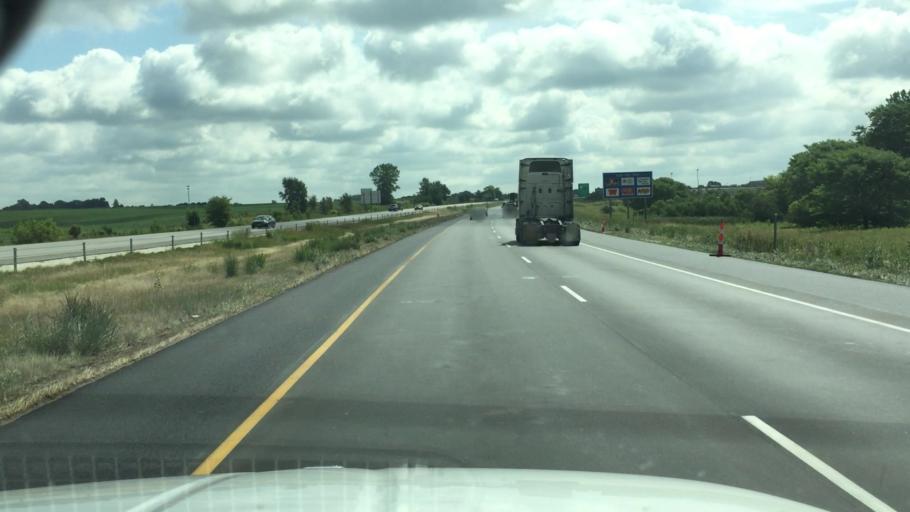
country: US
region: Iowa
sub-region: Scott County
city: Eldridge
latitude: 41.5996
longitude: -90.5947
